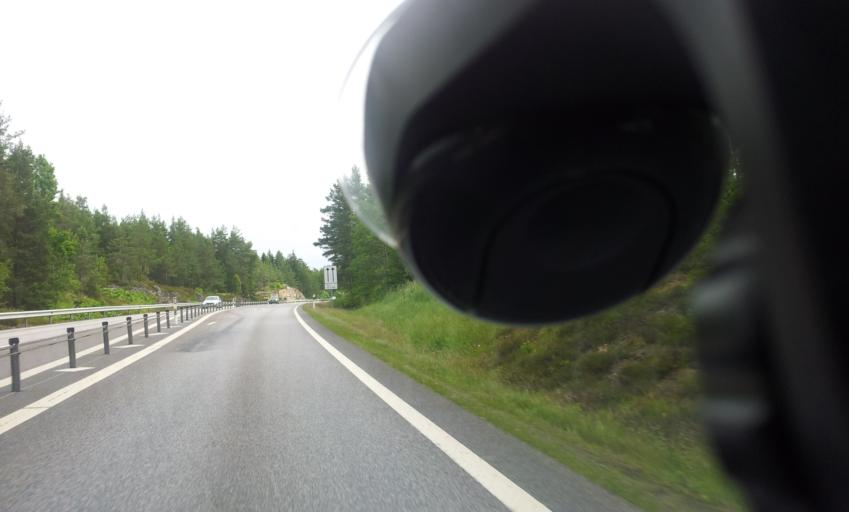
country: SE
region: OEstergoetland
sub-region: Valdemarsviks Kommun
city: Valdemarsvik
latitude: 58.0927
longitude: 16.5250
